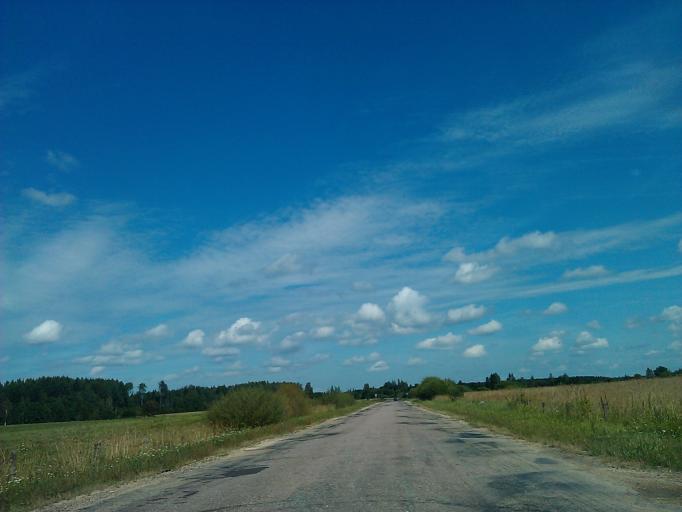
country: LV
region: Ropazu
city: Ropazi
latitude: 56.9184
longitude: 24.6178
